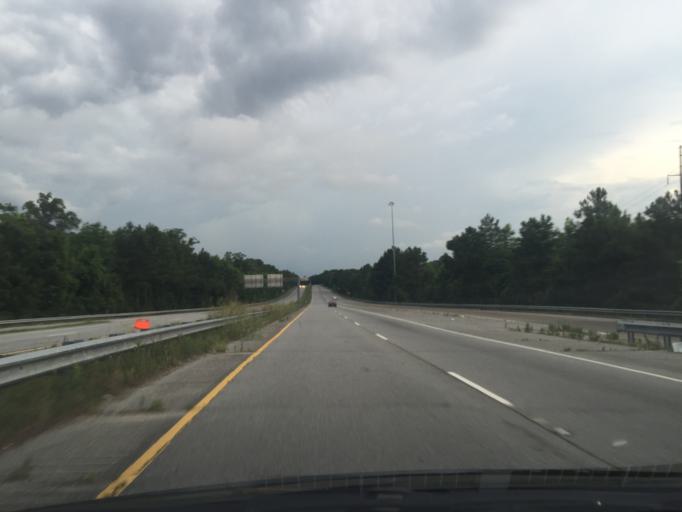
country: US
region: Georgia
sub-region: Chatham County
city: Savannah
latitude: 32.0419
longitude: -81.1490
